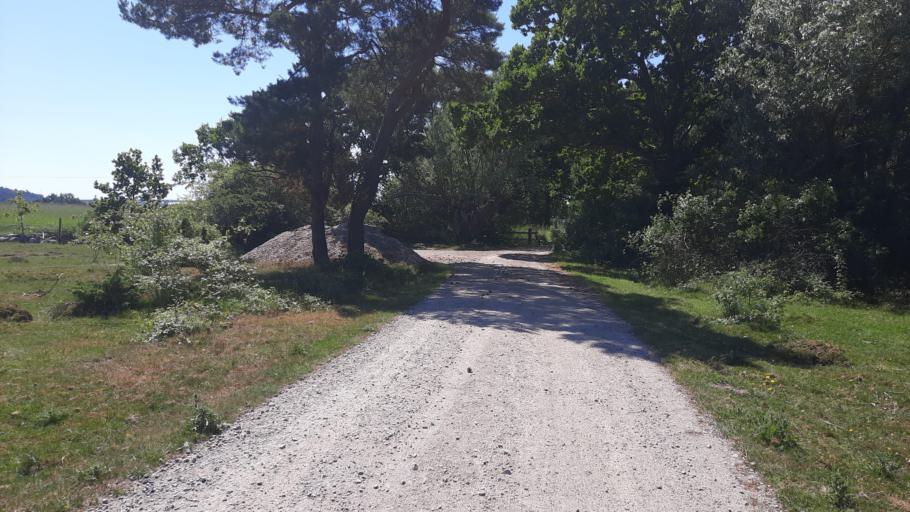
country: SE
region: Blekinge
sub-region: Karlskrona Kommun
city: Sturko
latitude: 56.1507
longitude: 15.7420
